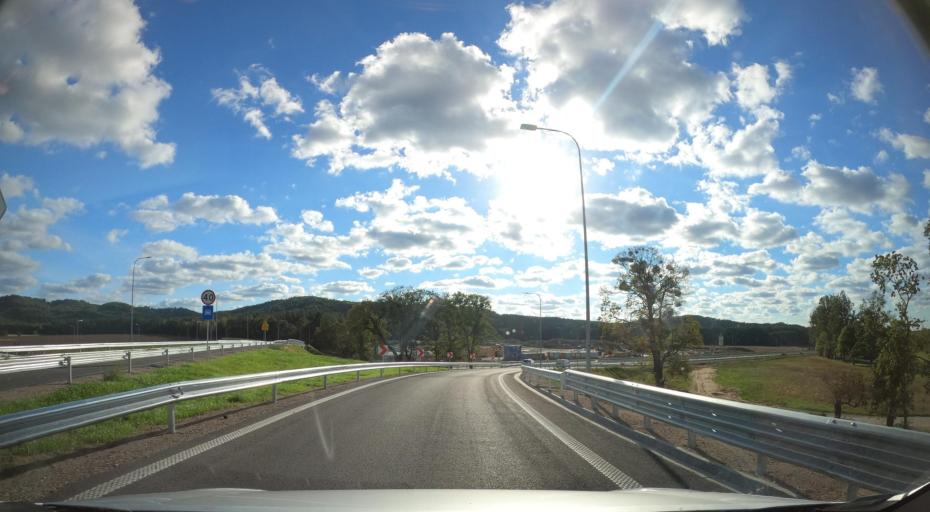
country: PL
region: Pomeranian Voivodeship
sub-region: Powiat wejherowski
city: Leczyce
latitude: 54.5687
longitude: 17.9654
